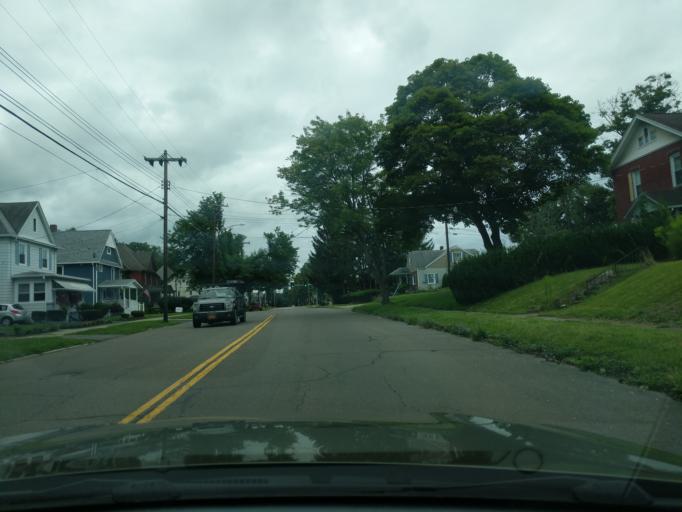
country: US
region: New York
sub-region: Chemung County
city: Elmira
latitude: 42.1030
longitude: -76.8177
